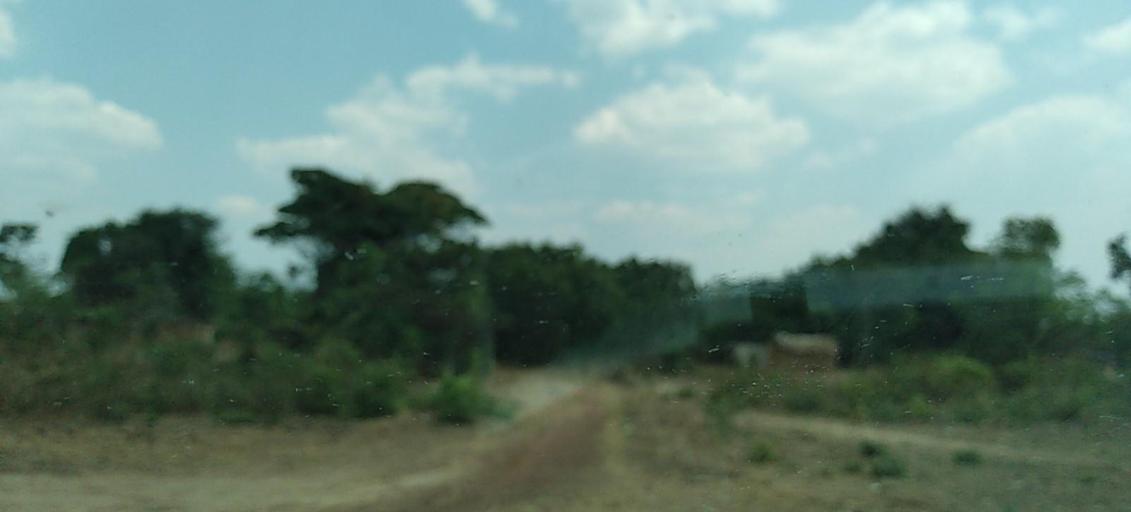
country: CD
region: Katanga
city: Kipushi
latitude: -11.9871
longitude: 27.4160
